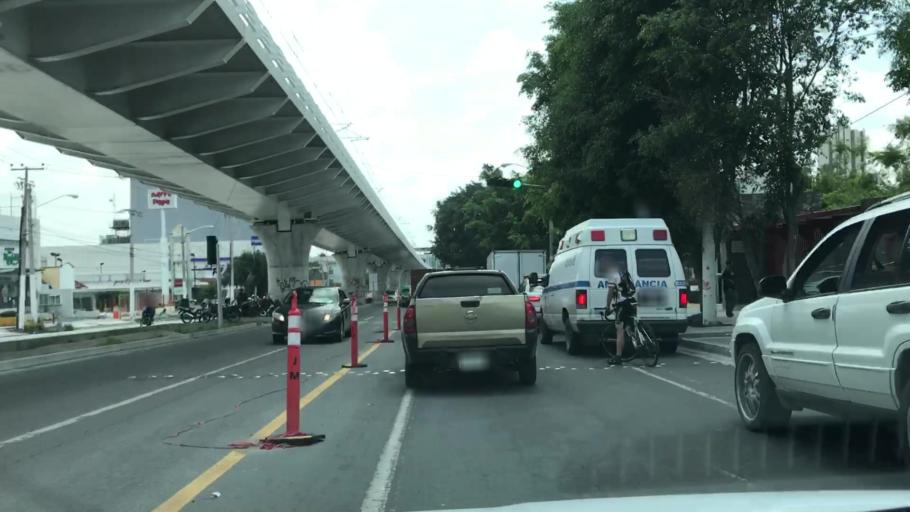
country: MX
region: Jalisco
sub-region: Zapopan
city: Zapopan
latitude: 20.7164
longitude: -103.3816
